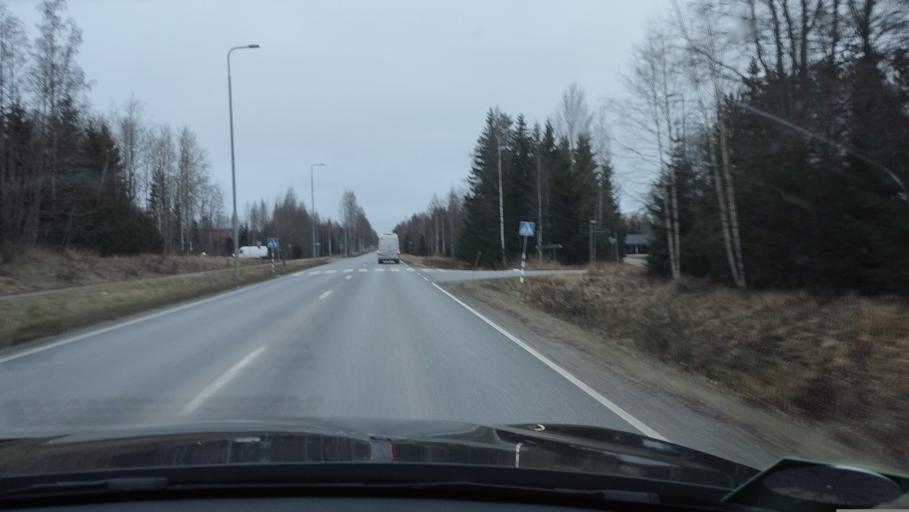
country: FI
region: Southern Ostrobothnia
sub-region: Suupohja
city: Kauhajoki
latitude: 62.4091
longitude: 22.1665
